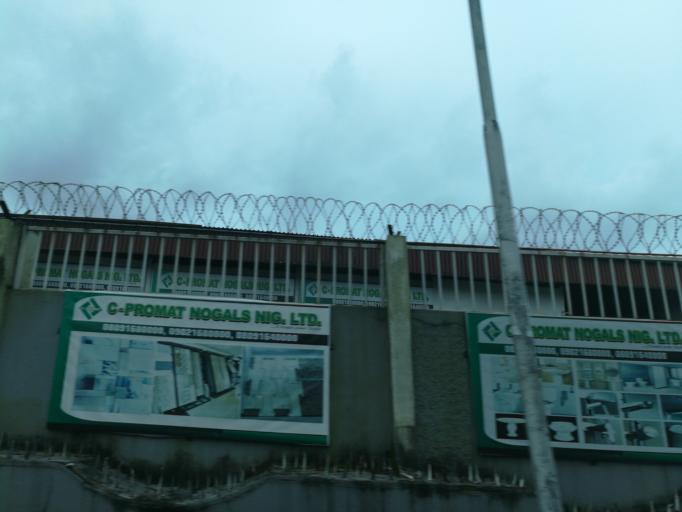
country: NG
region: Rivers
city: Port Harcourt
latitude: 4.8201
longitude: 6.9935
